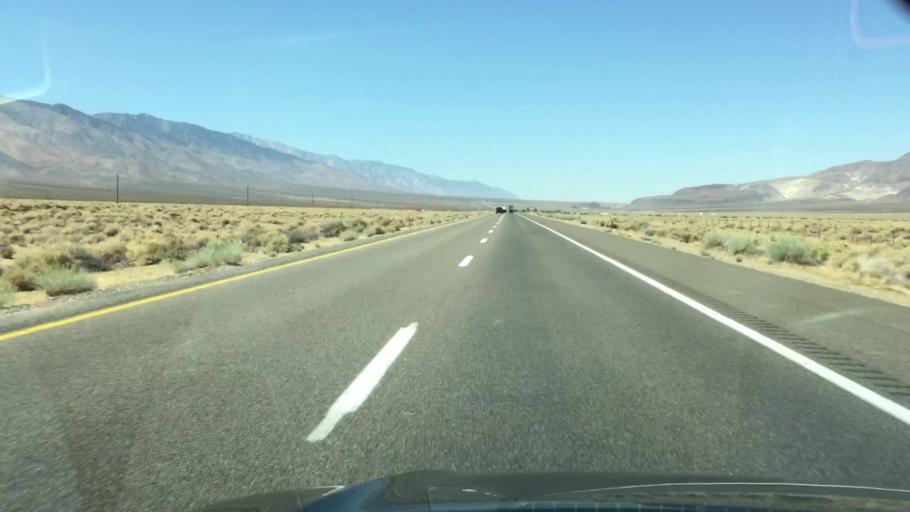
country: US
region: California
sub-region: Kern County
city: Inyokern
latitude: 36.0253
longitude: -117.9406
